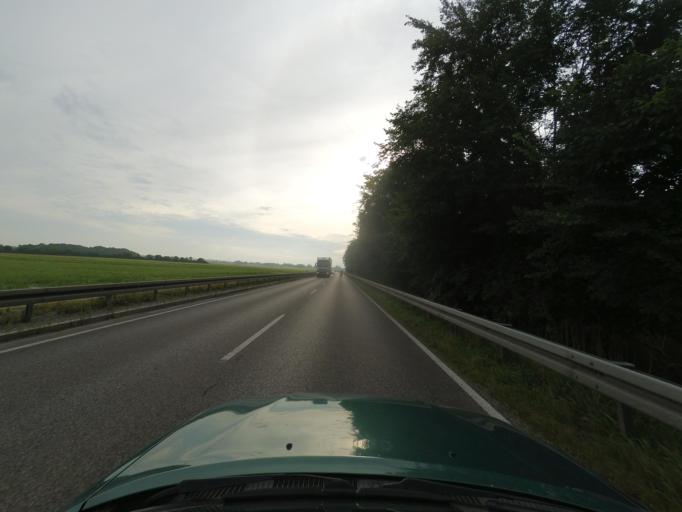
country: DE
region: Bavaria
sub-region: Upper Bavaria
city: Eichenau
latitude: 48.1509
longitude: 11.3216
